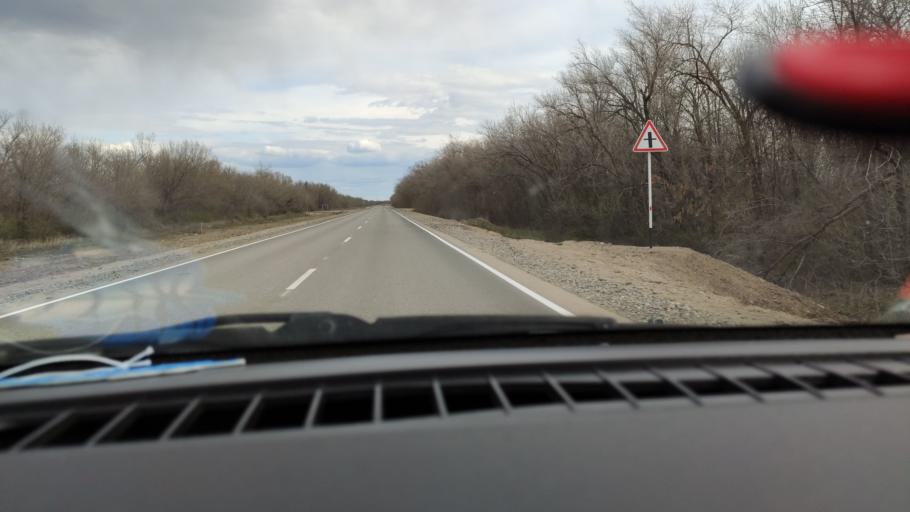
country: RU
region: Saratov
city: Privolzhskiy
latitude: 51.1641
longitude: 45.9501
